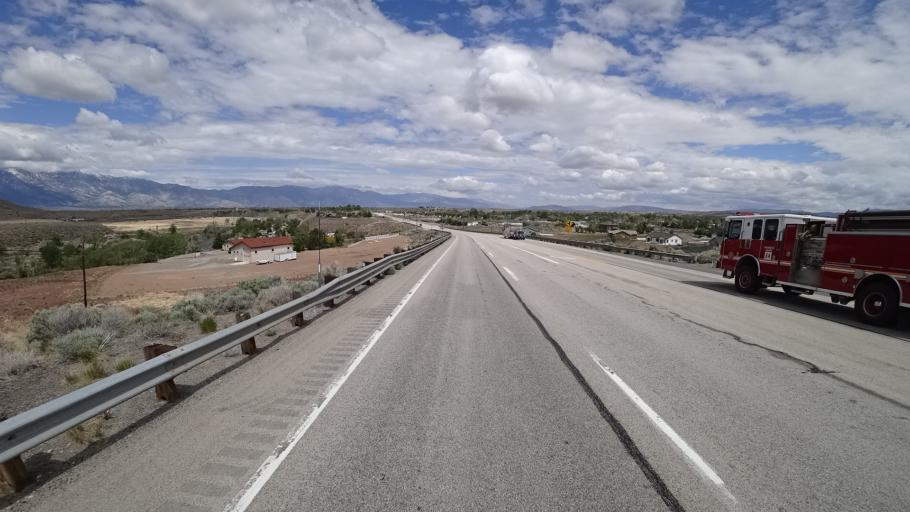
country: US
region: Nevada
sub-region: Douglas County
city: Gardnerville Ranchos
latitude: 38.8774
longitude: -119.6859
